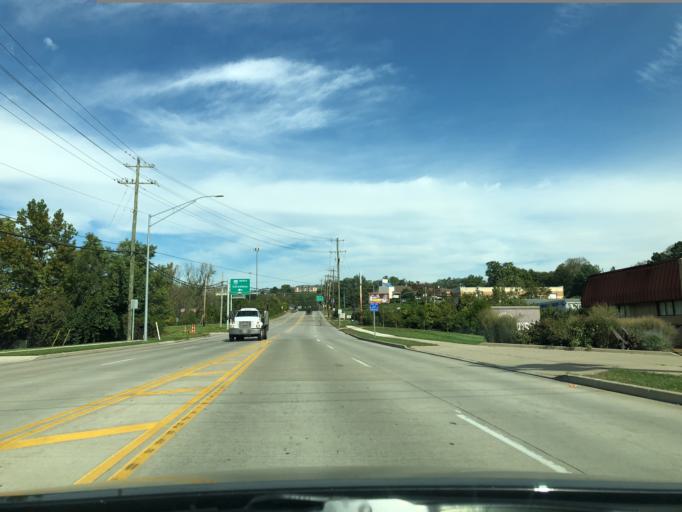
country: US
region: Ohio
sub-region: Hamilton County
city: Silverton
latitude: 39.1665
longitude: -84.4202
